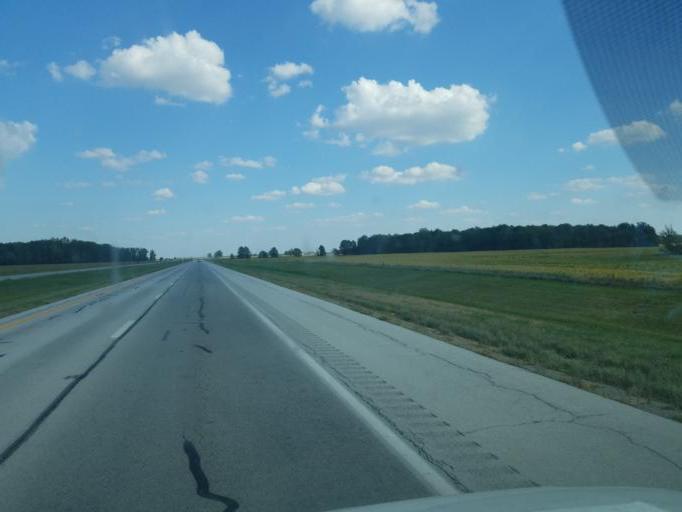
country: US
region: Ohio
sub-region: Hardin County
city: Forest
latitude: 40.8241
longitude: -83.4453
